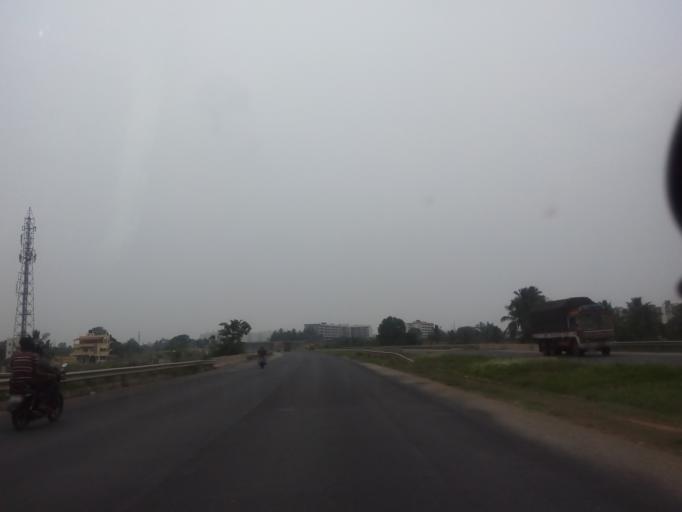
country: IN
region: Karnataka
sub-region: Bangalore Urban
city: Bangalore
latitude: 12.8661
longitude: 77.6297
